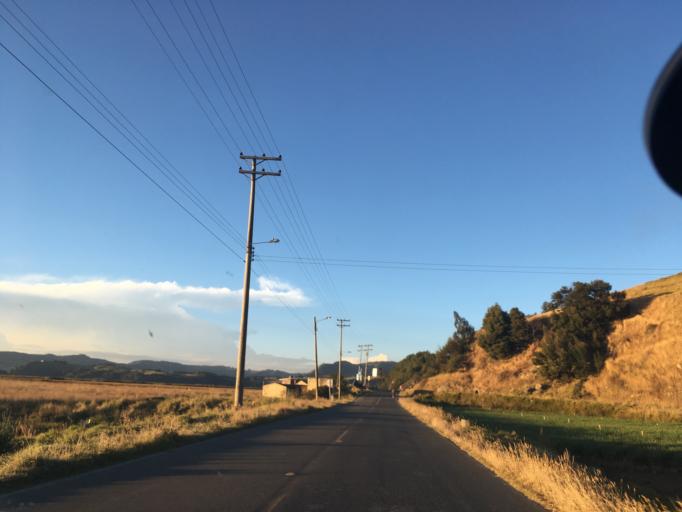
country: CO
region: Boyaca
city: Aquitania
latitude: 5.5352
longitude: -72.8848
